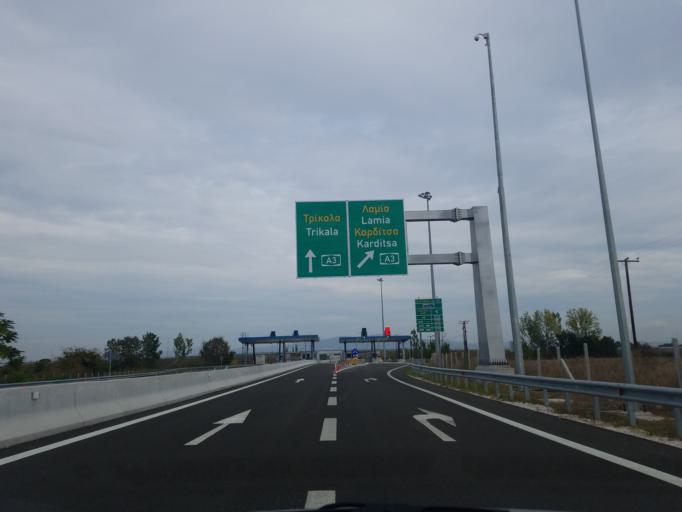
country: GR
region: Thessaly
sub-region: Nomos Kardhitsas
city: Agia Triada
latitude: 39.4733
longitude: 21.9031
